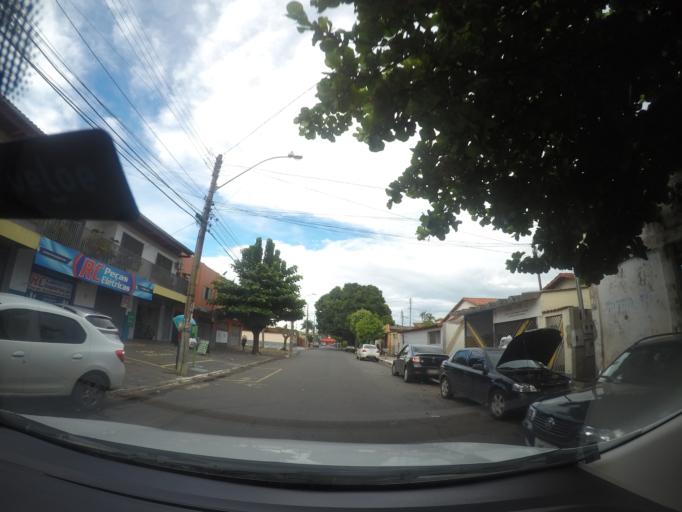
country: BR
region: Goias
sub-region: Goiania
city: Goiania
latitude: -16.6697
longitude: -49.2824
